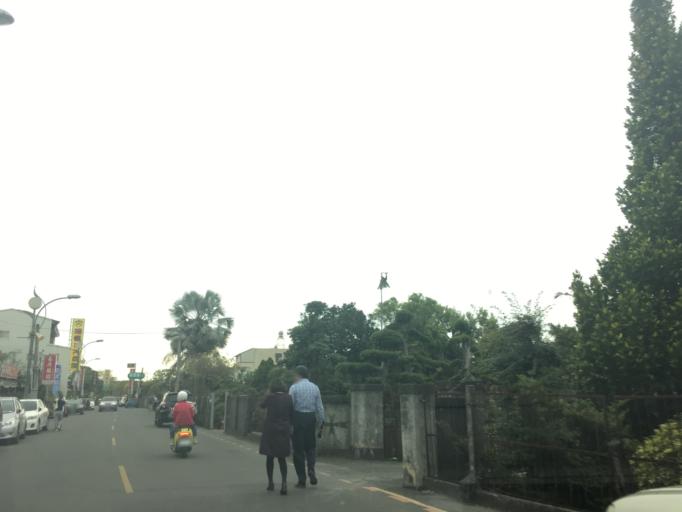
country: TW
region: Taiwan
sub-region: Nantou
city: Nantou
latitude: 23.9033
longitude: 120.5301
